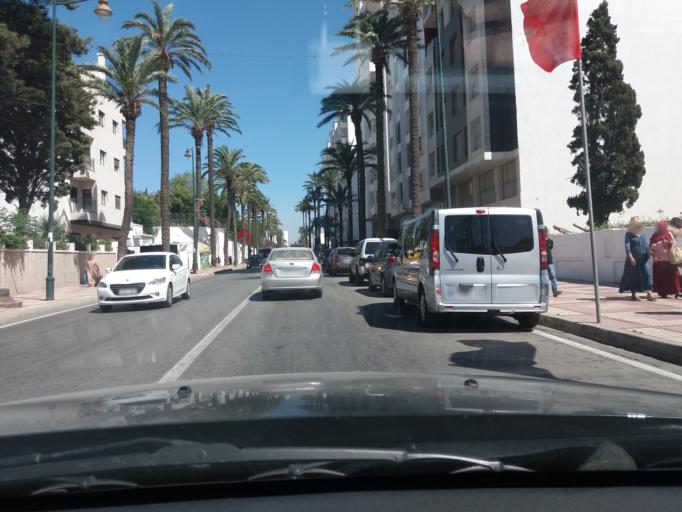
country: MA
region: Tanger-Tetouan
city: Tetouan
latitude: 35.5694
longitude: -5.3826
